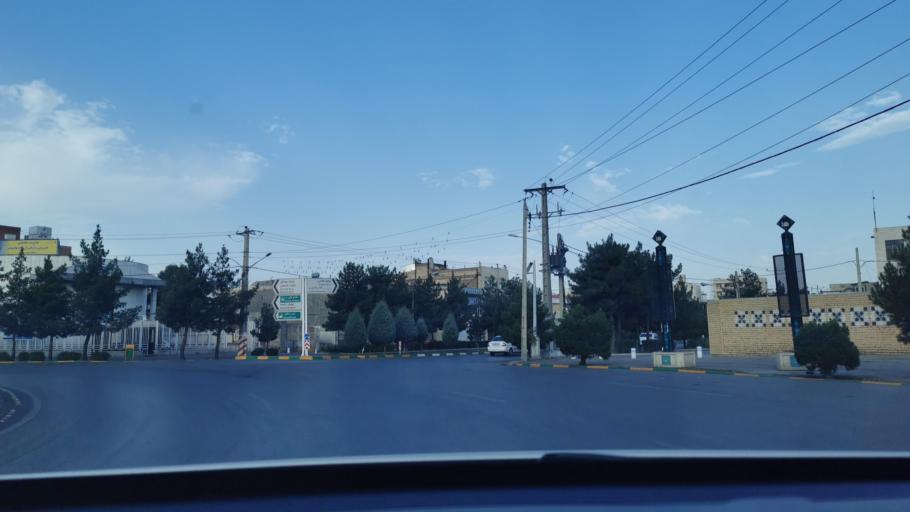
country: IR
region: Razavi Khorasan
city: Mashhad
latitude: 36.3595
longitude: 59.5128
